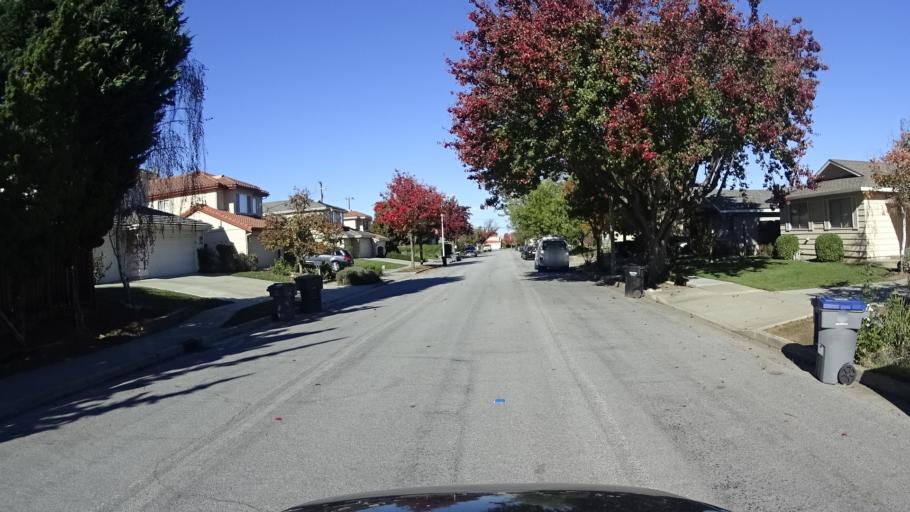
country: US
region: California
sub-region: Santa Clara County
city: Cupertino
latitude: 37.3394
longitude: -122.0208
